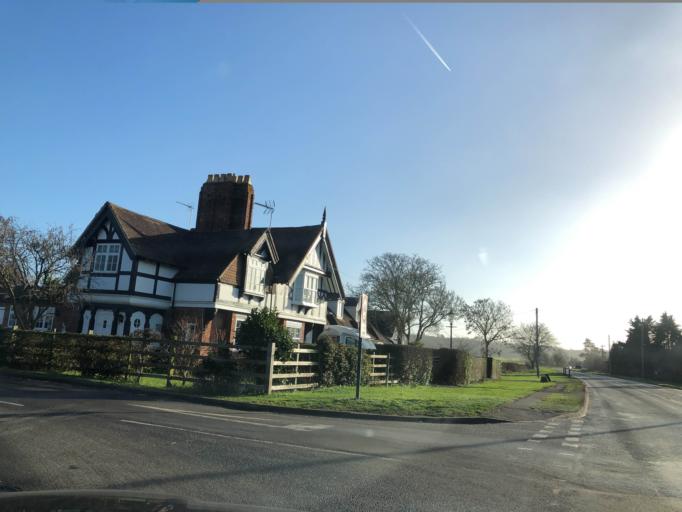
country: GB
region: England
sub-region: Warwickshire
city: Wellesbourne Mountford
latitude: 52.1913
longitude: -1.5860
